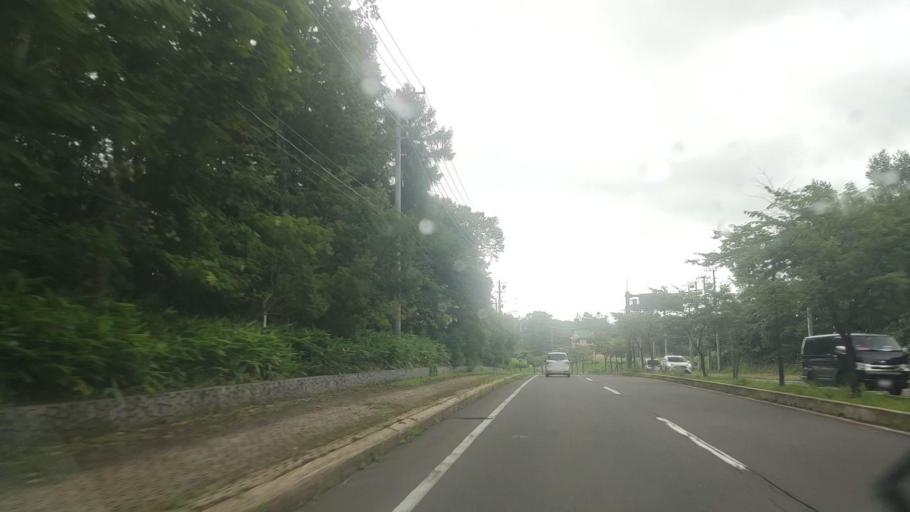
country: JP
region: Hokkaido
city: Shiraoi
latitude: 42.4732
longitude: 141.1480
